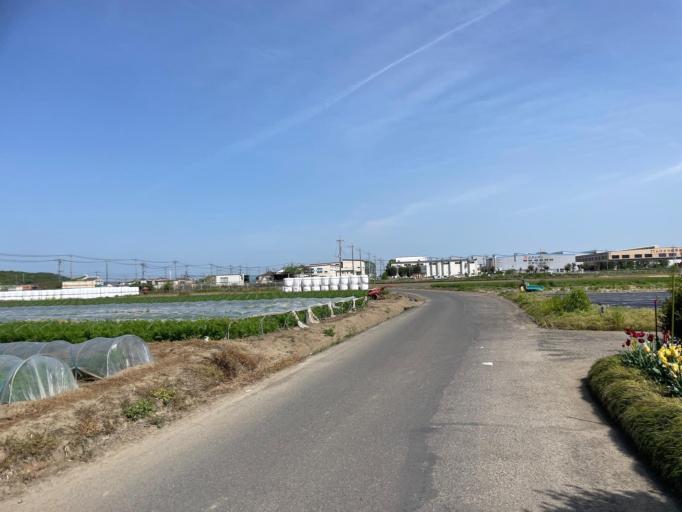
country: JP
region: Gunma
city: Tatebayashi
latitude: 36.3062
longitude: 139.5064
